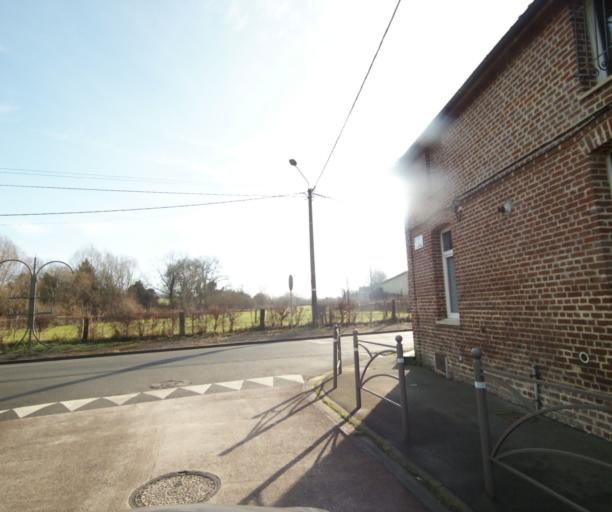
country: FR
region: Nord-Pas-de-Calais
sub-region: Departement du Nord
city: Maing
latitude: 50.3101
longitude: 3.4970
